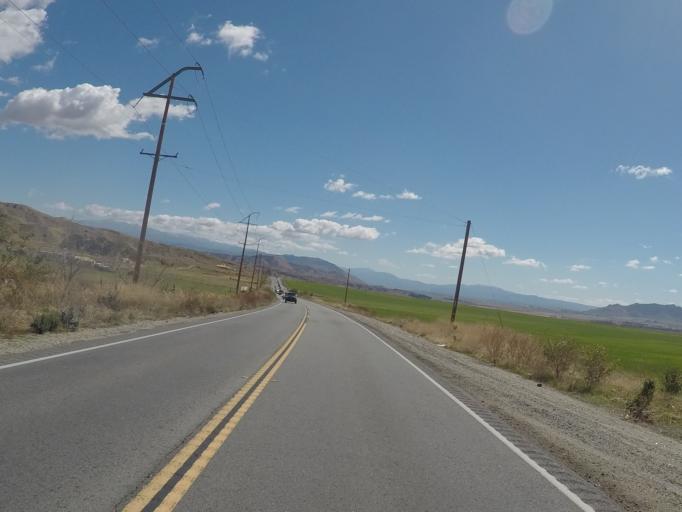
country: US
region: California
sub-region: Riverside County
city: Lakeview
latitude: 33.9277
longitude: -117.1200
